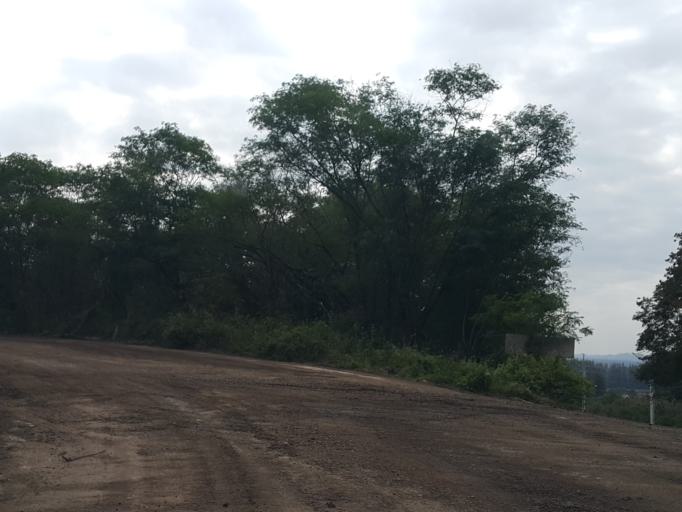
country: TH
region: Lampang
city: Mae Mo
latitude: 18.3149
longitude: 99.7465
